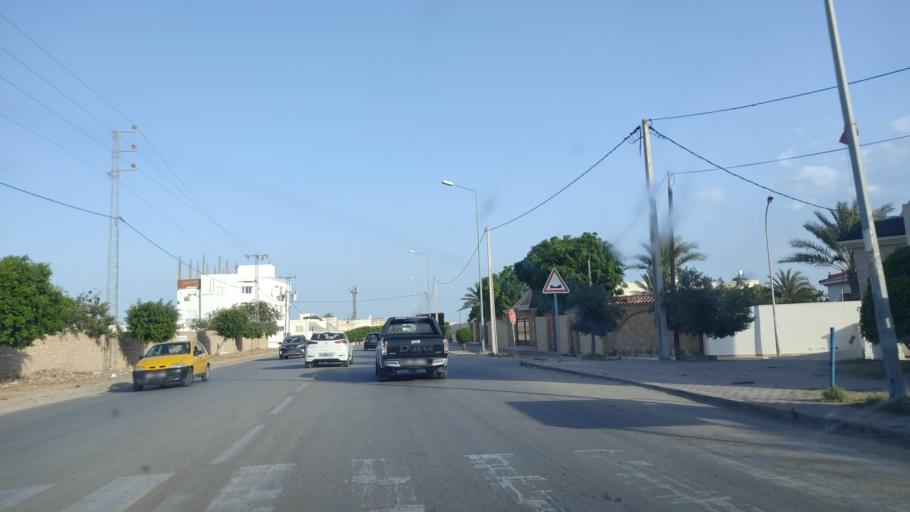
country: TN
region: Safaqis
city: Sfax
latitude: 34.7912
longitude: 10.6868
